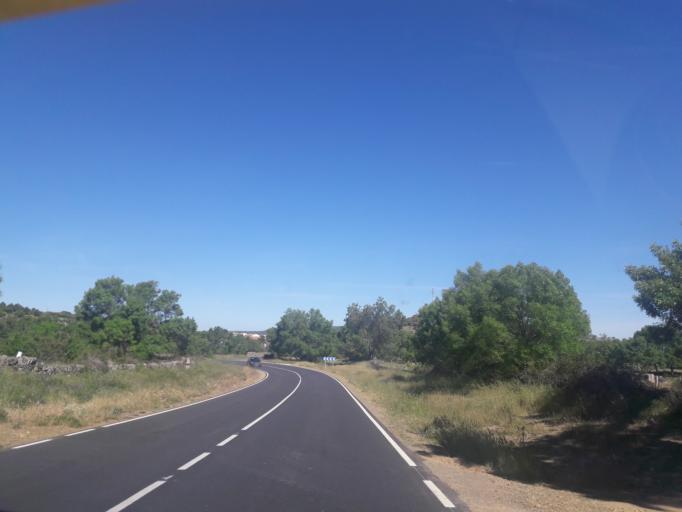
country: ES
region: Castille and Leon
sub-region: Provincia de Salamanca
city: Nava de Bejar
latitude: 40.4926
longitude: -5.6577
